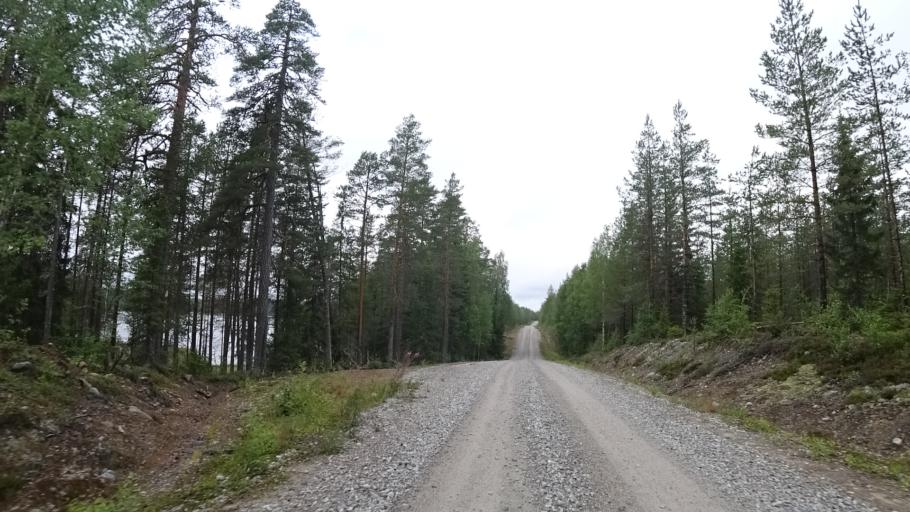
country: FI
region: North Karelia
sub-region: Pielisen Karjala
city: Lieksa
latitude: 63.4666
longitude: 30.2907
